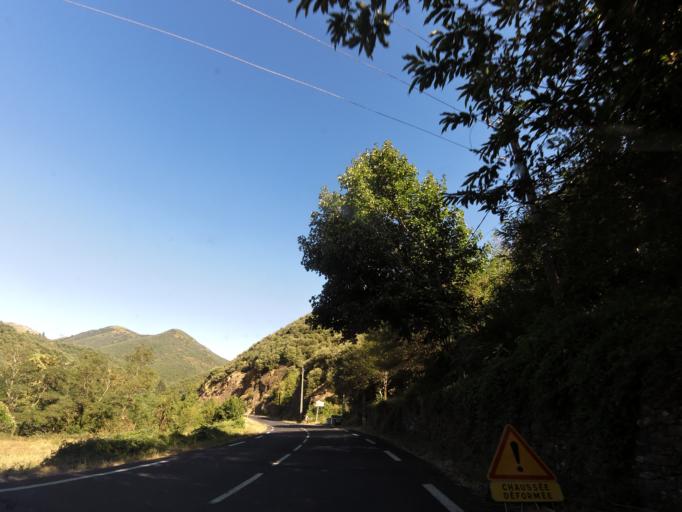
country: FR
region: Languedoc-Roussillon
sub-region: Departement du Gard
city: Valleraugue
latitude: 44.0784
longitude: 3.6526
